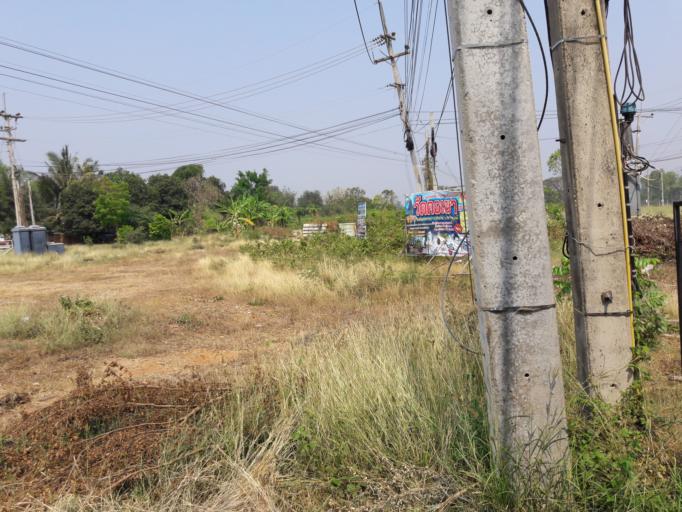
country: TH
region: Kanchanaburi
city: Kanchanaburi
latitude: 14.0326
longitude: 99.5023
